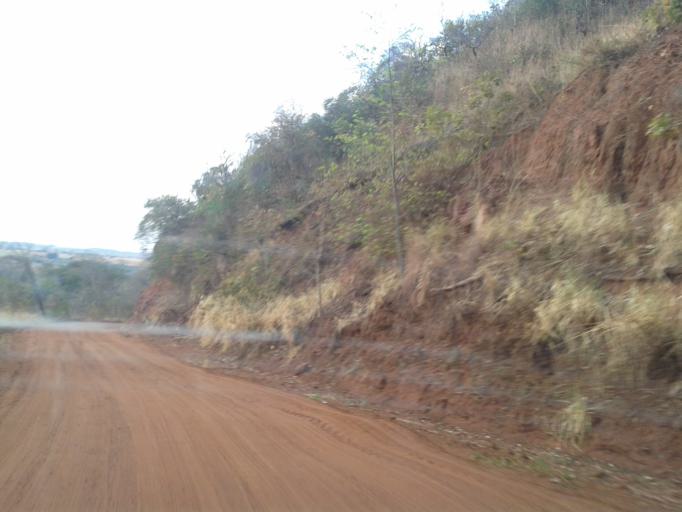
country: BR
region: Minas Gerais
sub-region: Santa Vitoria
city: Santa Vitoria
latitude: -19.1813
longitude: -49.8583
